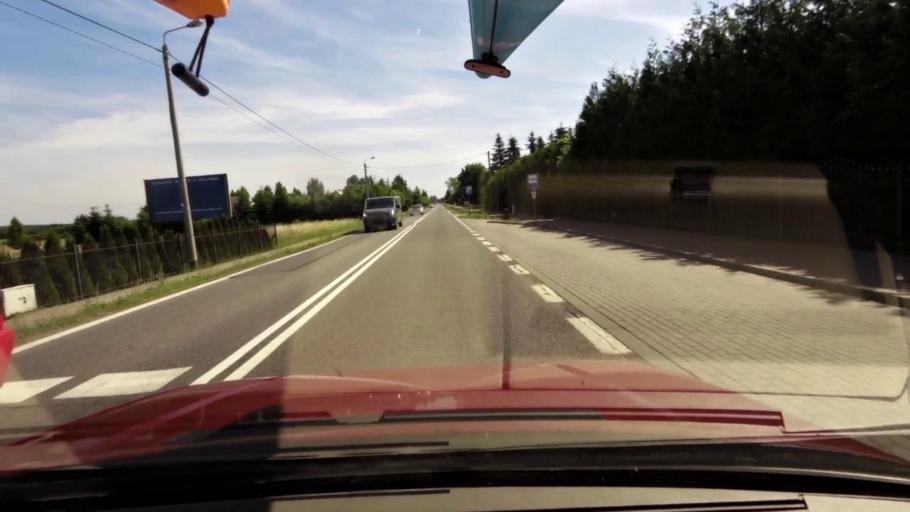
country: PL
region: Pomeranian Voivodeship
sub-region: Powiat slupski
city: Kobylnica
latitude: 54.4229
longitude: 17.0073
